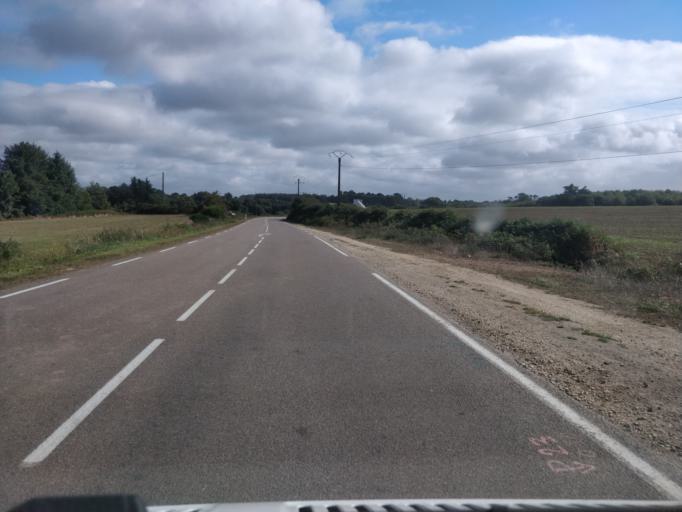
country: FR
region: Brittany
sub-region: Departement du Finistere
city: Landudec
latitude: 47.9964
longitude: -4.3767
